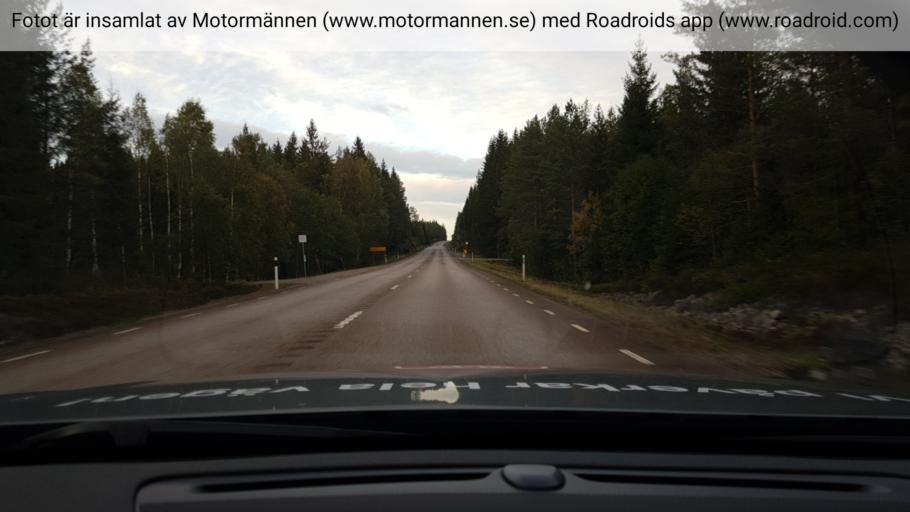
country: SE
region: Vaestra Goetaland
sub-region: Amals Kommun
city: Amal
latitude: 59.0646
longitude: 12.5476
